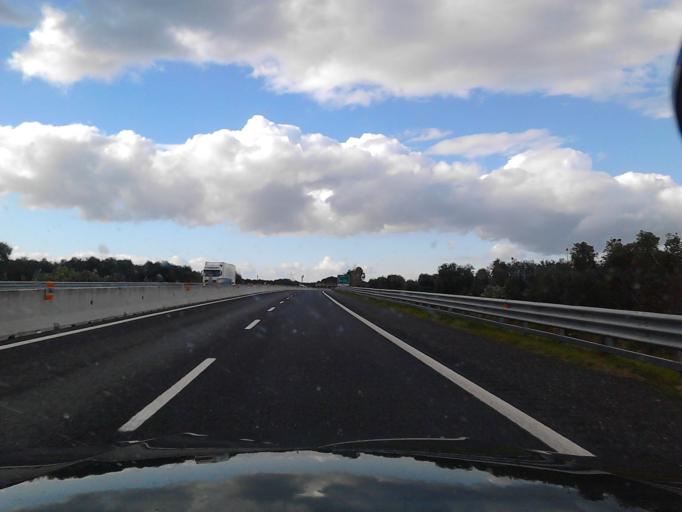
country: IT
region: Apulia
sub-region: Provincia di Barletta - Andria - Trani
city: Andria
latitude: 41.2524
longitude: 16.3005
